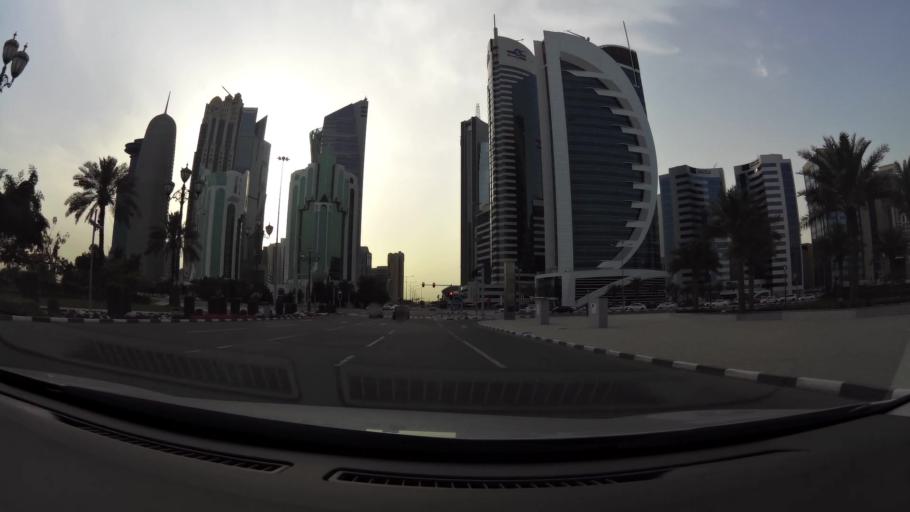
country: QA
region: Baladiyat ad Dawhah
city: Doha
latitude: 25.3190
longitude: 51.5329
